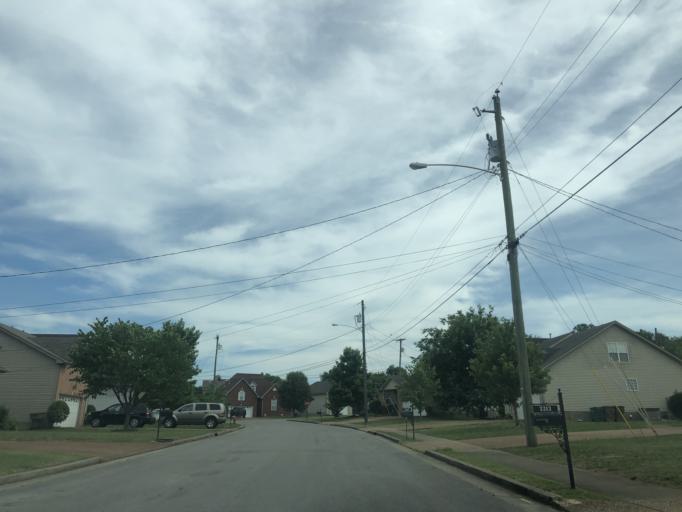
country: US
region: Tennessee
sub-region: Davidson County
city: Nashville
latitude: 36.2129
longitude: -86.8133
